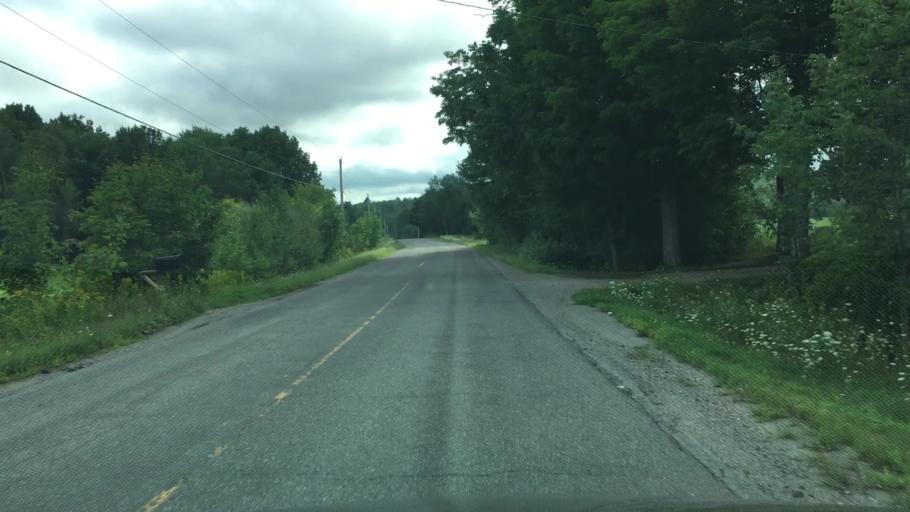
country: US
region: Maine
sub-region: Penobscot County
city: Hampden
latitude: 44.7200
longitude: -68.8673
